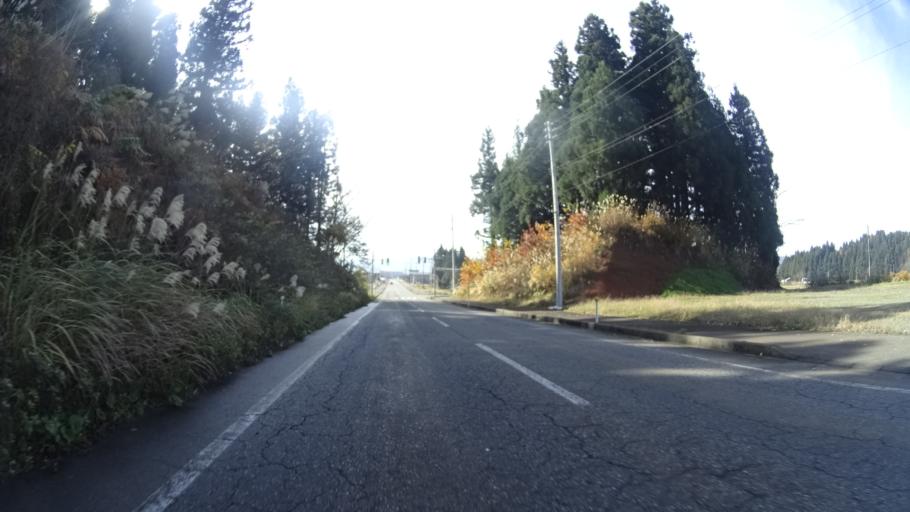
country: JP
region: Niigata
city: Muikamachi
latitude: 37.1804
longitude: 138.9771
